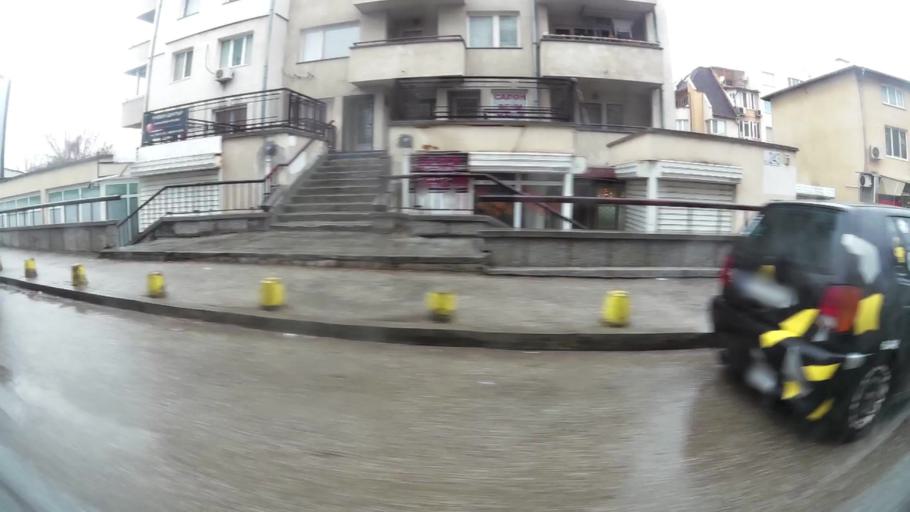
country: BG
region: Sofia-Capital
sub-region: Stolichna Obshtina
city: Sofia
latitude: 42.6419
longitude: 23.3666
